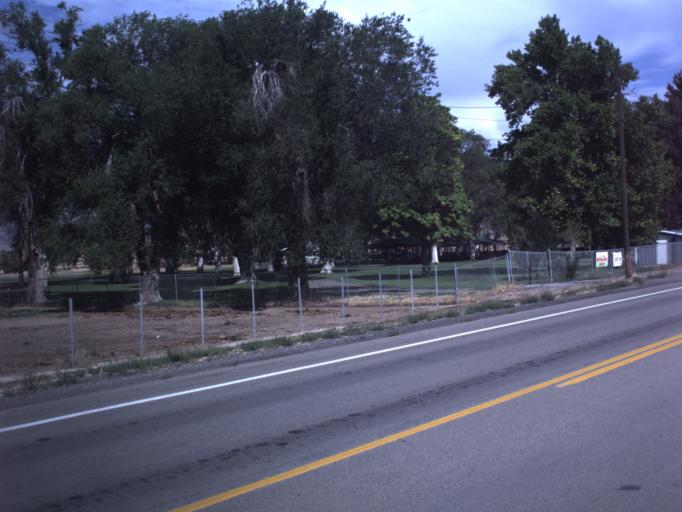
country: US
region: Utah
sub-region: Juab County
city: Nephi
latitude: 39.5621
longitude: -111.8619
